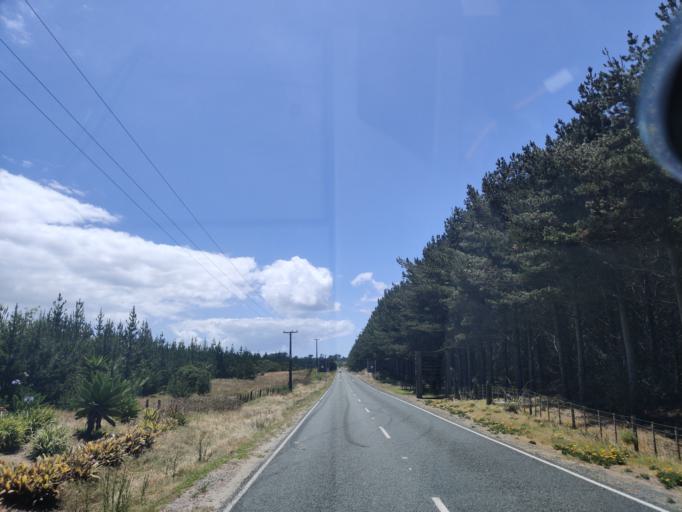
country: NZ
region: Northland
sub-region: Far North District
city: Kaitaia
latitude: -35.0370
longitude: 173.1750
